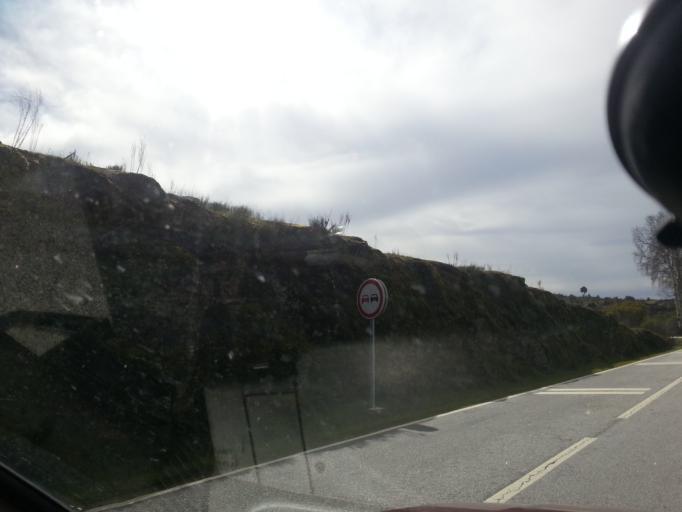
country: PT
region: Guarda
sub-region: Fornos de Algodres
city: Fornos de Algodres
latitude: 40.5829
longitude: -7.5419
